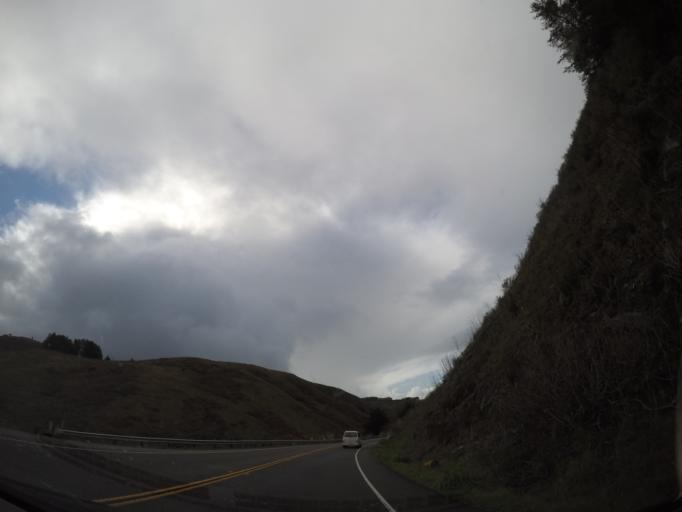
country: US
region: California
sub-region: Sonoma County
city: Bodega Bay
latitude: 38.3207
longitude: -123.0133
